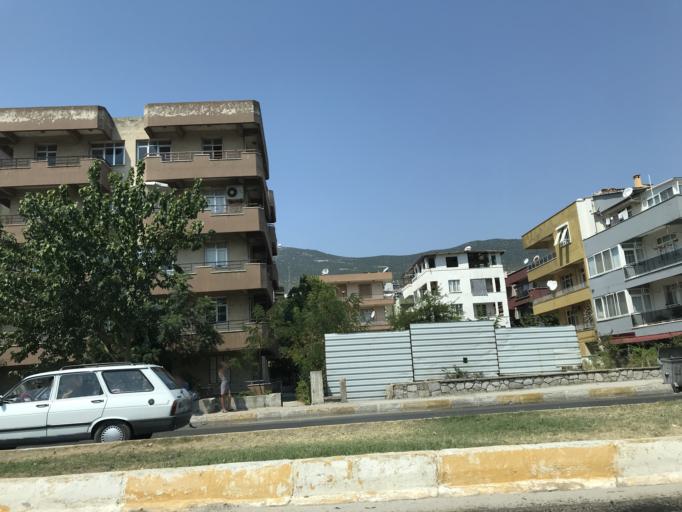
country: TR
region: Mugla
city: Milas
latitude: 37.2996
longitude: 27.7813
